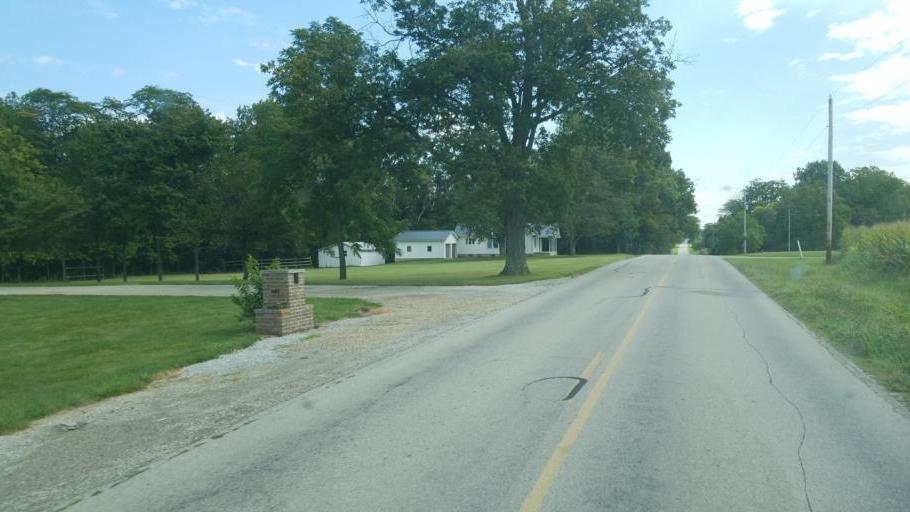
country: US
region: Ohio
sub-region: Seneca County
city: Tiffin
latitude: 41.0658
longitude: -83.1238
